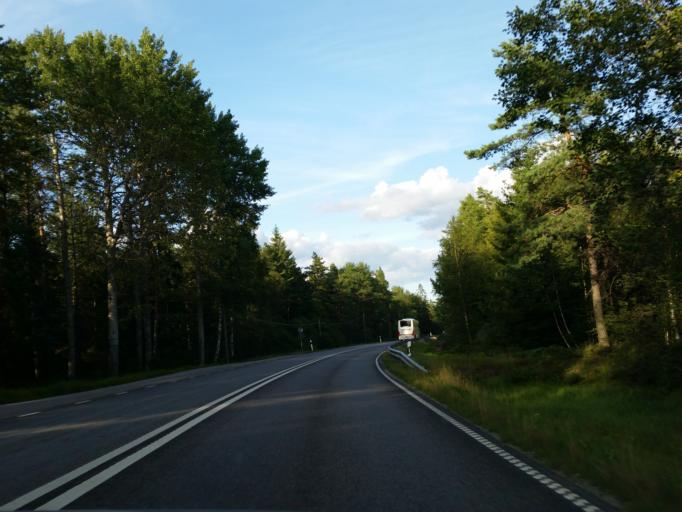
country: SE
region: Stockholm
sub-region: Sodertalje Kommun
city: Molnbo
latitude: 59.0575
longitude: 17.4669
